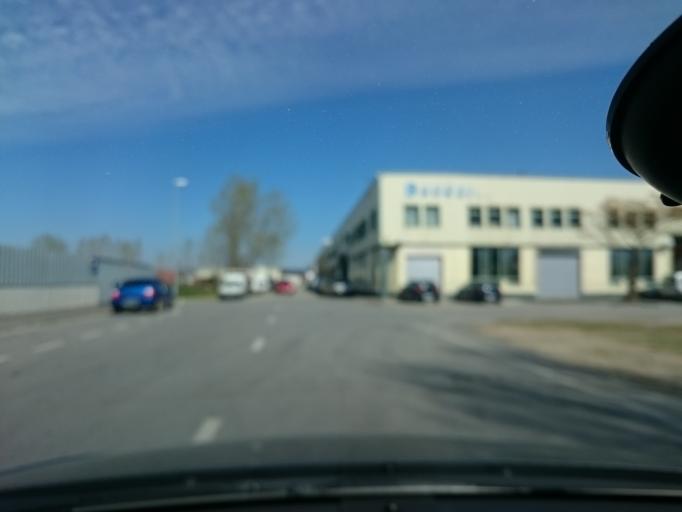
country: ES
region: Castille and Leon
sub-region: Provincia de Leon
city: Camponaraya
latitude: 42.5647
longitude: -6.6408
